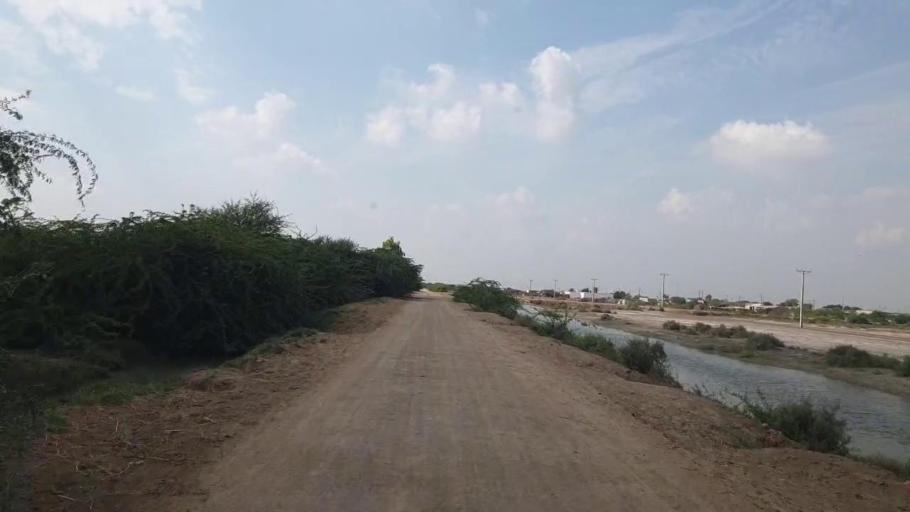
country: PK
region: Sindh
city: Badin
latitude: 24.5065
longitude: 68.6475
